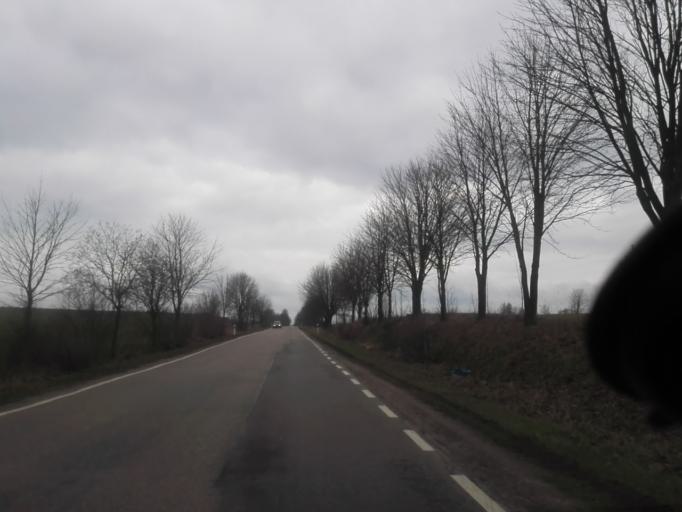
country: PL
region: Podlasie
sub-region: Suwalki
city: Suwalki
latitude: 54.2380
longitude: 22.9153
